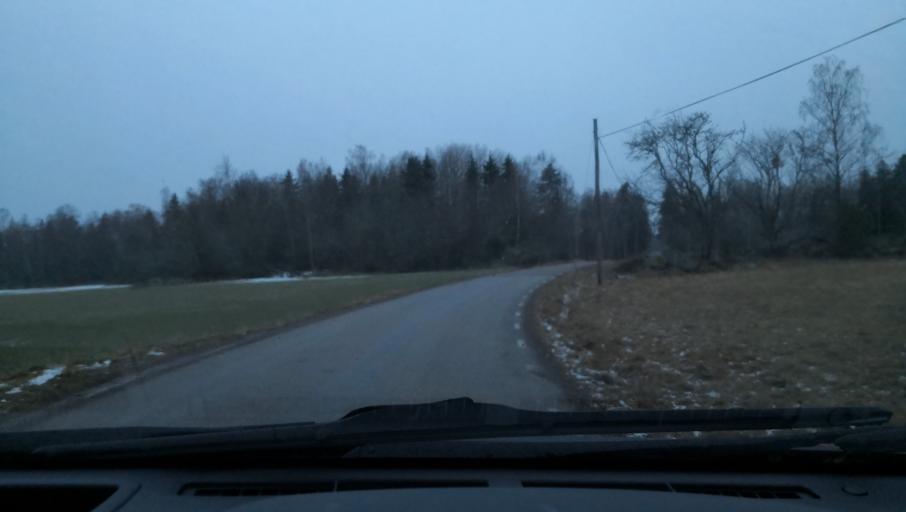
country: SE
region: Uppsala
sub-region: Enkopings Kommun
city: Hummelsta
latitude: 59.4541
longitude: 16.8236
